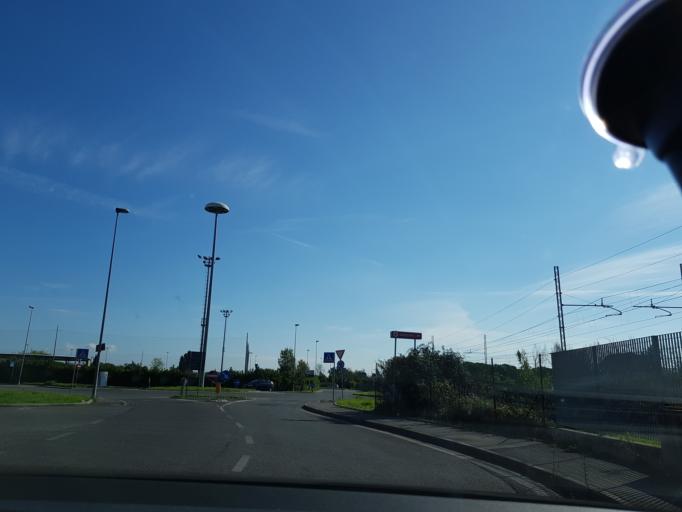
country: IT
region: Tuscany
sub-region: Province of Florence
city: Empoli
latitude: 43.7130
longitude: 10.9251
